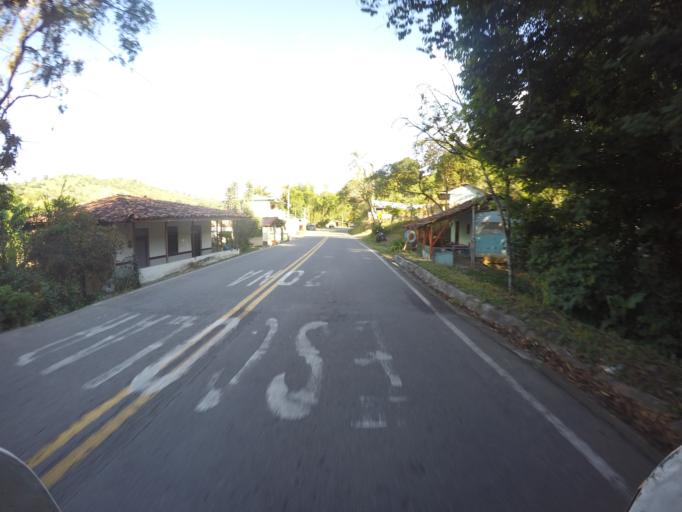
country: CO
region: Valle del Cauca
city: Cartago
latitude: 4.7108
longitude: -75.8581
